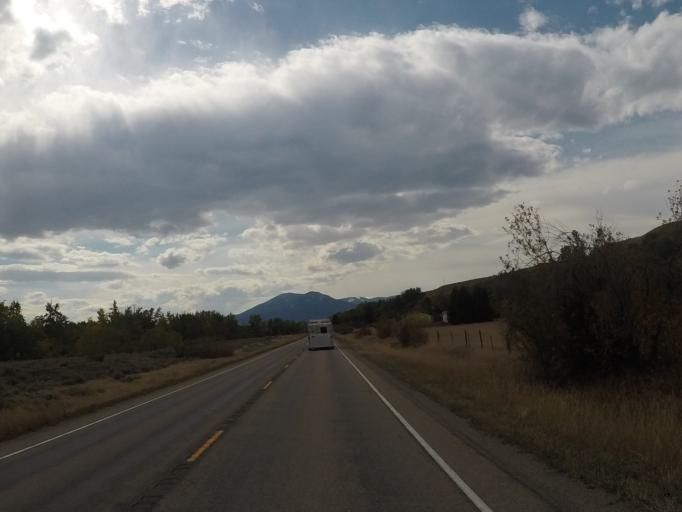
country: US
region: Montana
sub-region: Carbon County
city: Red Lodge
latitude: 45.2359
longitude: -109.2372
